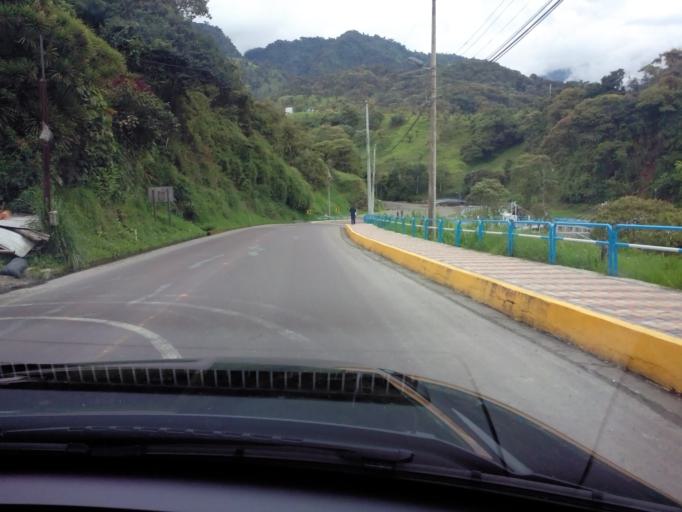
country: EC
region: Napo
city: Archidona
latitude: -0.4652
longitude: -77.8931
